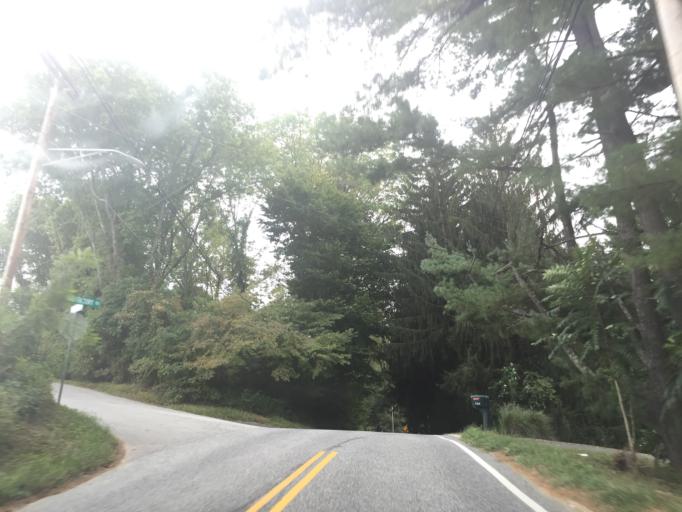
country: US
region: Maryland
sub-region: Harford County
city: Bel Air South
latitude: 39.5005
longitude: -76.3510
